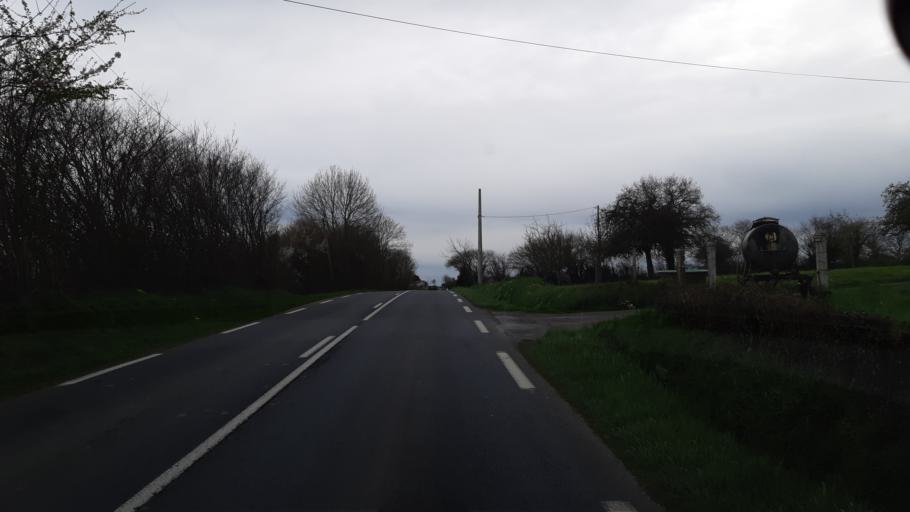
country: FR
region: Lower Normandy
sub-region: Departement de la Manche
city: Percy
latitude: 49.0037
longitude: -1.1525
